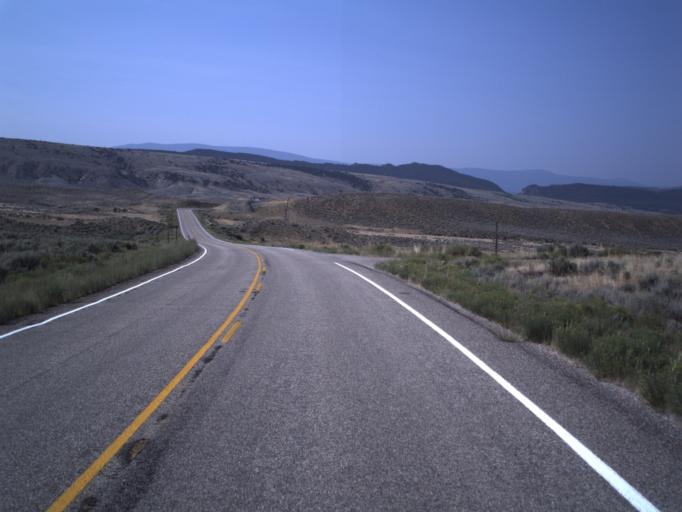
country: US
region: Utah
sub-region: Daggett County
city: Manila
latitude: 40.9920
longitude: -109.4358
